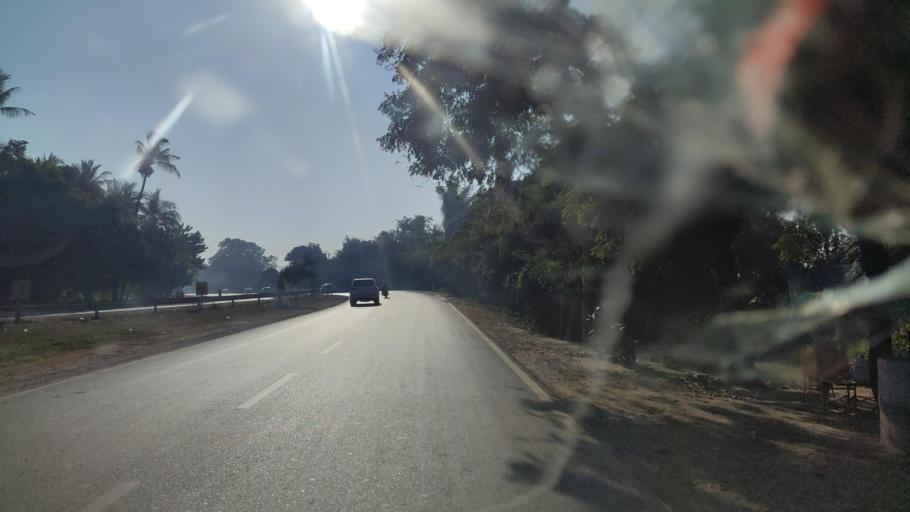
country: MM
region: Mandalay
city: Mandalay
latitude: 21.9116
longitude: 96.1723
